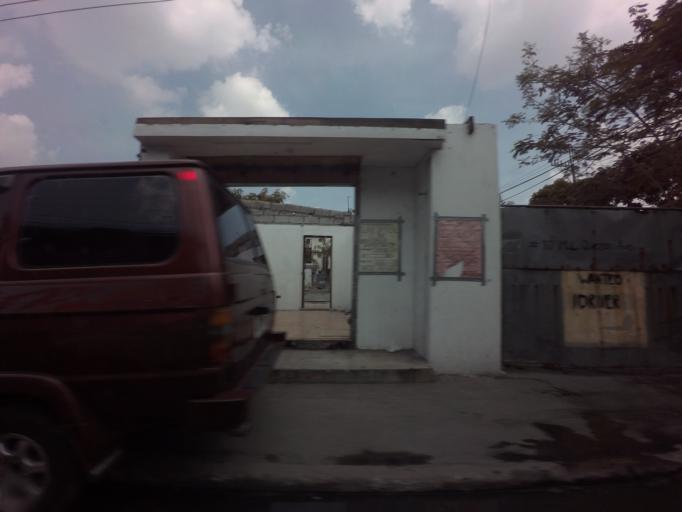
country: PH
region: Calabarzon
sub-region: Province of Rizal
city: Taguig
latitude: 14.5189
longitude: 121.0735
